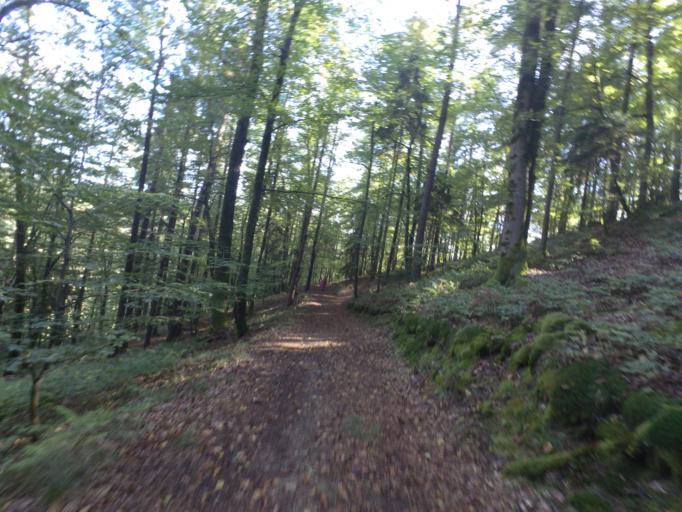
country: AT
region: Styria
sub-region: Politischer Bezirk Leibnitz
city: Kitzeck im Sausal
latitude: 46.7691
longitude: 15.4415
